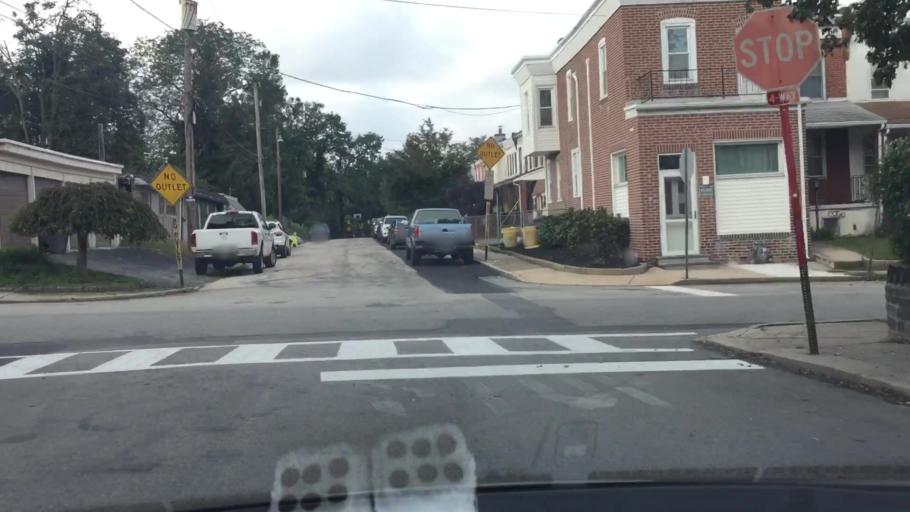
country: US
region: Pennsylvania
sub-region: Montgomery County
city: Narberth
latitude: 40.0095
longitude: -75.2598
